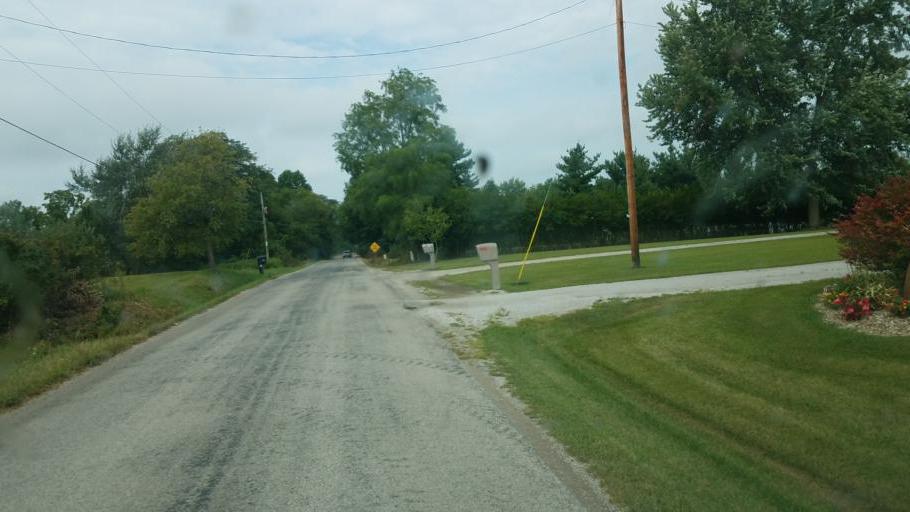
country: US
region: Ohio
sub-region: Morrow County
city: Mount Gilead
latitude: 40.4413
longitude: -82.7825
